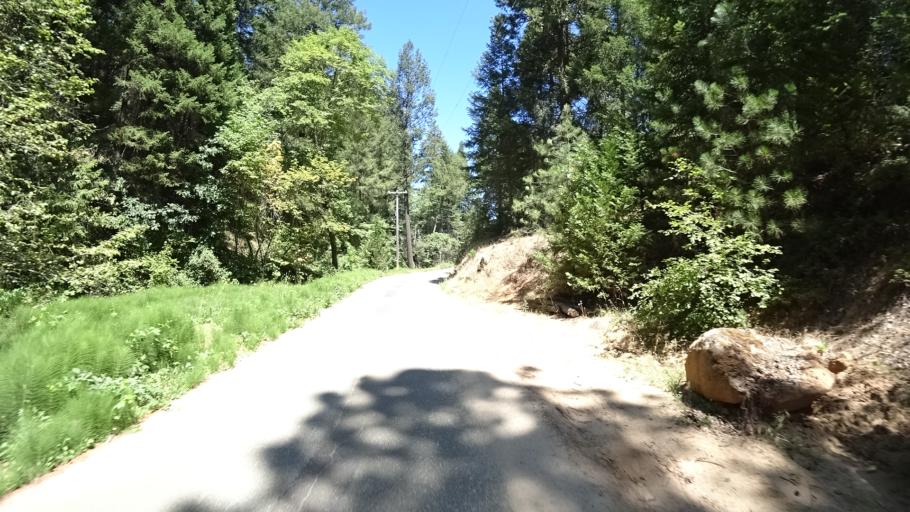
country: US
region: California
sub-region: Amador County
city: Pioneer
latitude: 38.4090
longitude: -120.5234
